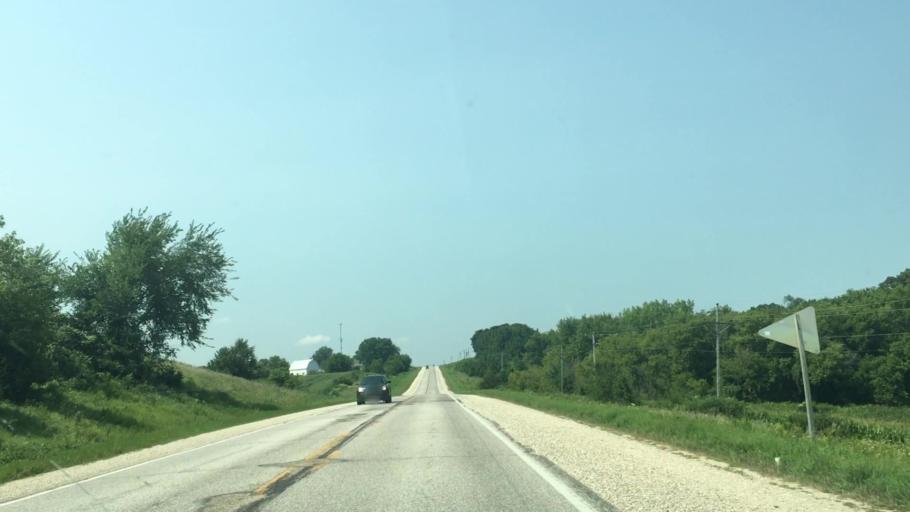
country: US
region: Iowa
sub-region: Fayette County
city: West Union
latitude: 43.0836
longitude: -91.8462
